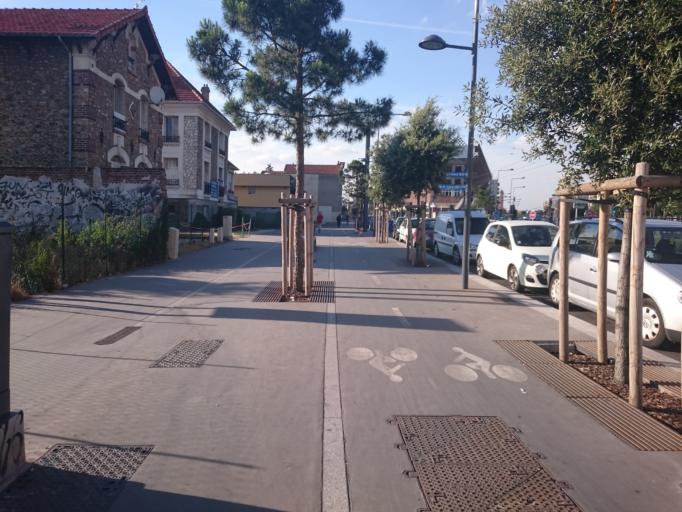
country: FR
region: Ile-de-France
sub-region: Departement du Val-de-Marne
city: Villejuif
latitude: 48.7856
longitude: 2.3668
